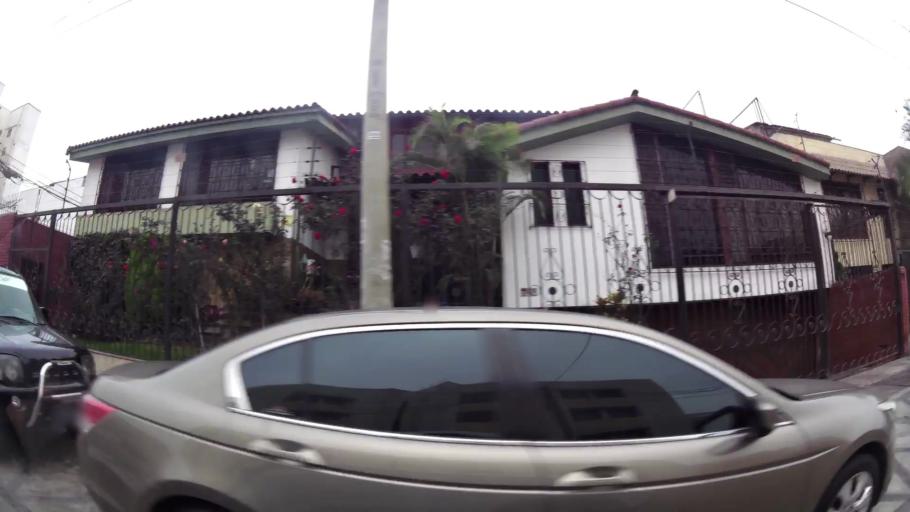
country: PE
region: Lima
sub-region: Lima
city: San Luis
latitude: -12.1022
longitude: -77.0045
